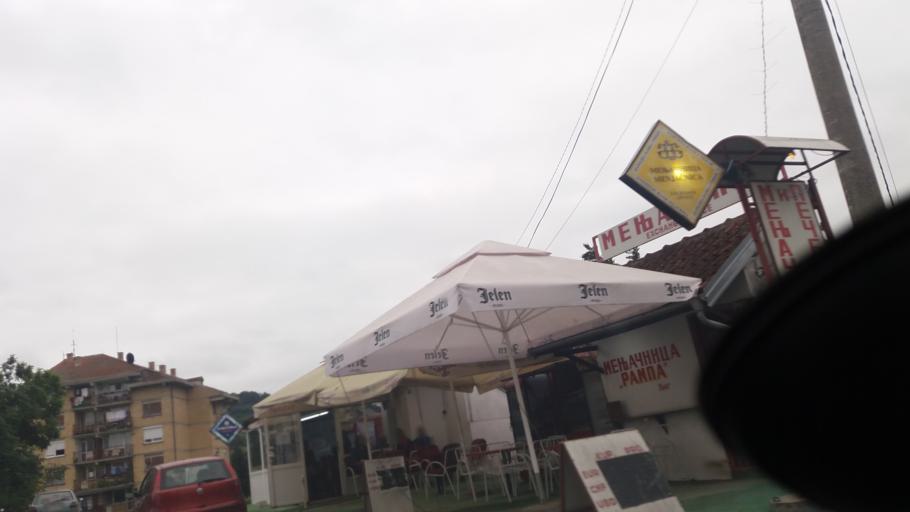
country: RS
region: Central Serbia
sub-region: Kolubarski Okrug
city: Ljig
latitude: 44.2268
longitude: 20.2363
